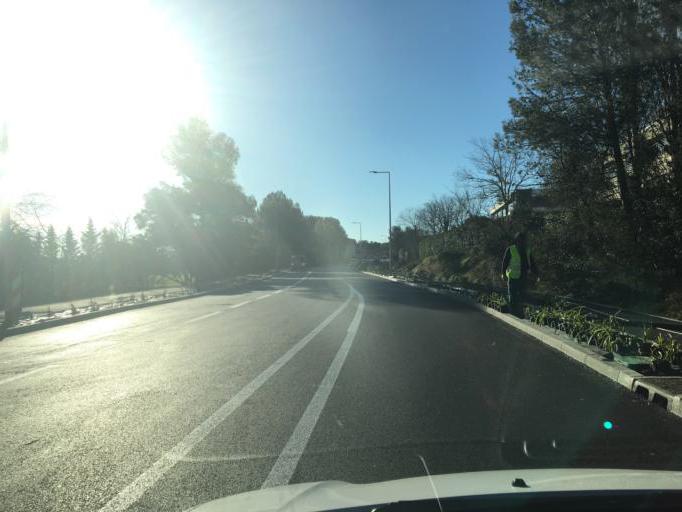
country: FR
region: Provence-Alpes-Cote d'Azur
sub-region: Departement des Bouches-du-Rhone
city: Cabries
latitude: 43.4844
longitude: 5.3632
